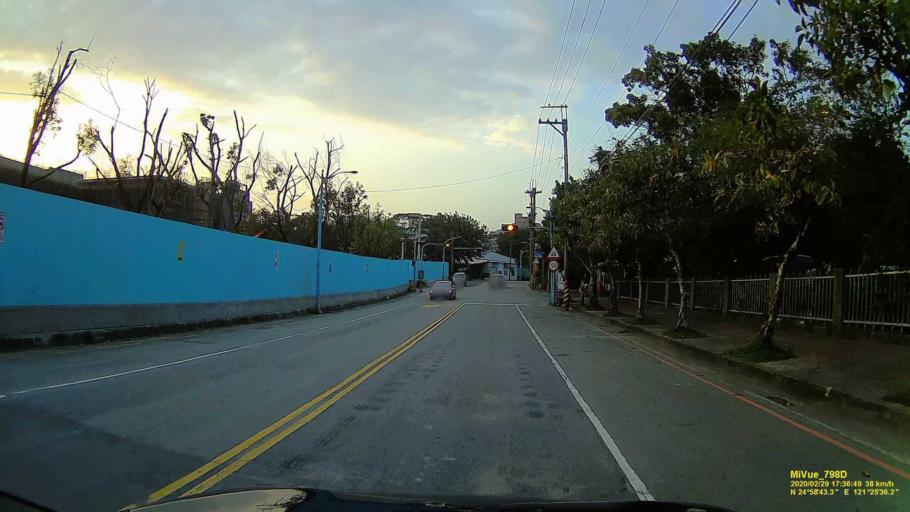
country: TW
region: Taipei
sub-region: Taipei
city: Banqiao
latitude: 24.9789
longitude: 121.4265
